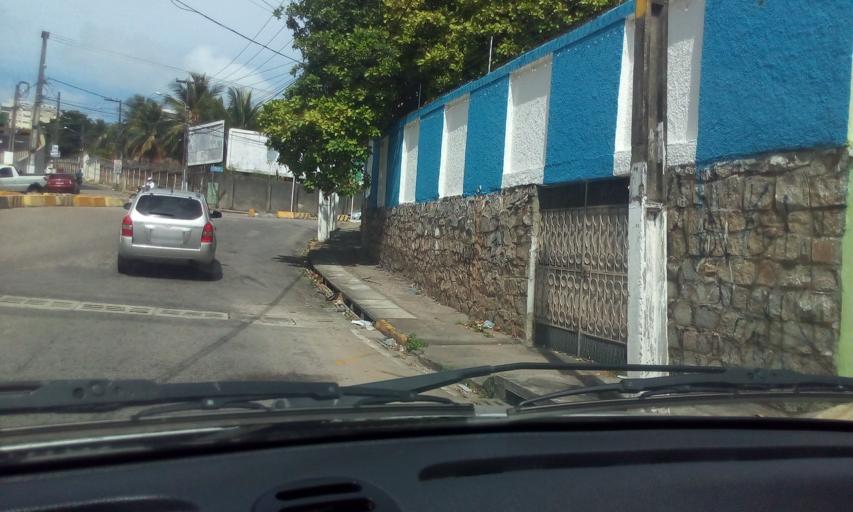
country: BR
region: Rio Grande do Norte
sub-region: Natal
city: Natal
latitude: -5.7930
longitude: -35.2070
